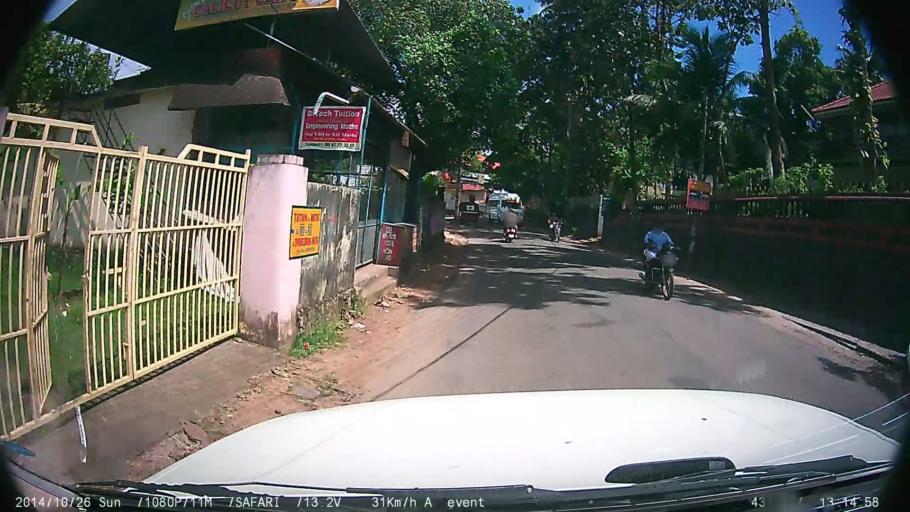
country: IN
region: Kerala
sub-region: Kottayam
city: Changanacheri
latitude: 9.4445
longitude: 76.5514
